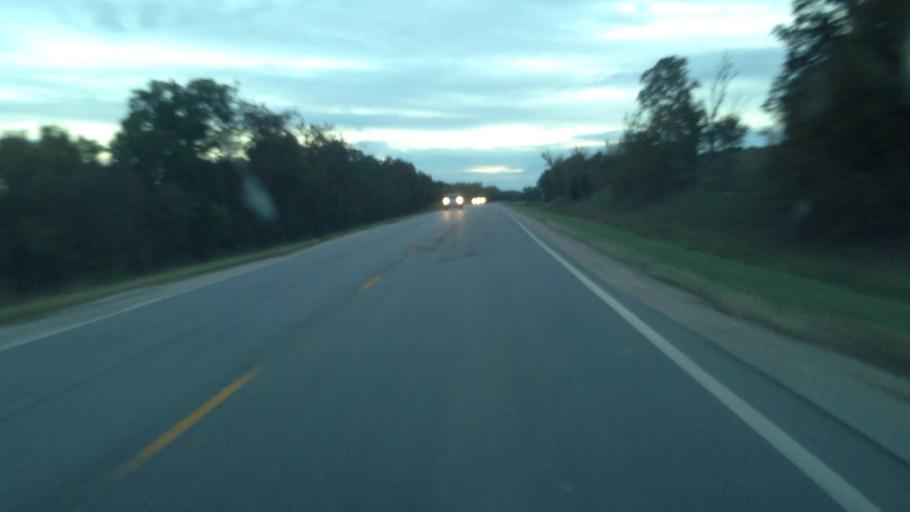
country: US
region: Kansas
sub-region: Anderson County
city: Garnett
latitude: 38.2081
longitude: -95.2490
